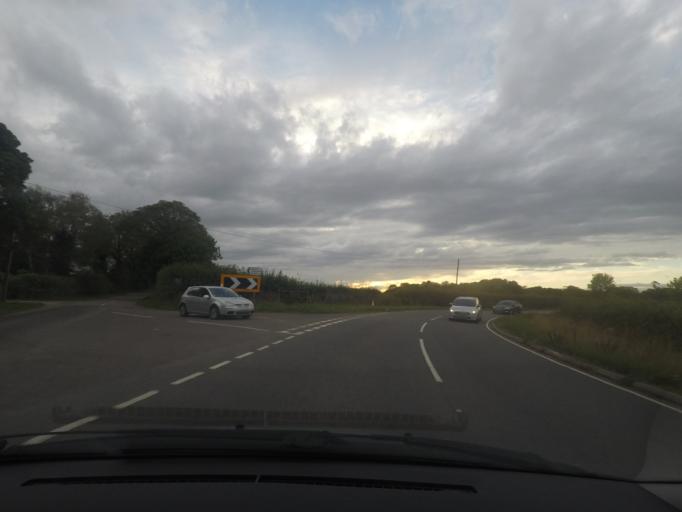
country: GB
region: England
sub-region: North East Lincolnshire
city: Wold Newton
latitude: 53.4338
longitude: -0.0670
